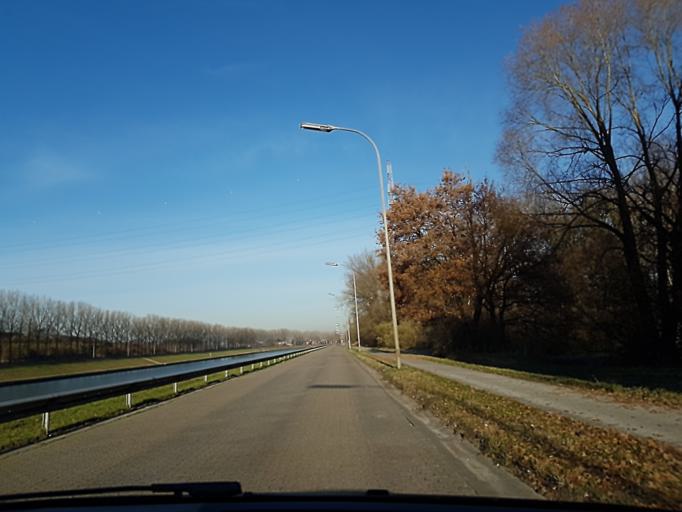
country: BE
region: Flanders
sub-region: Provincie Vlaams-Brabant
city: Kapelle-op-den-Bos
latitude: 51.0243
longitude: 4.3604
